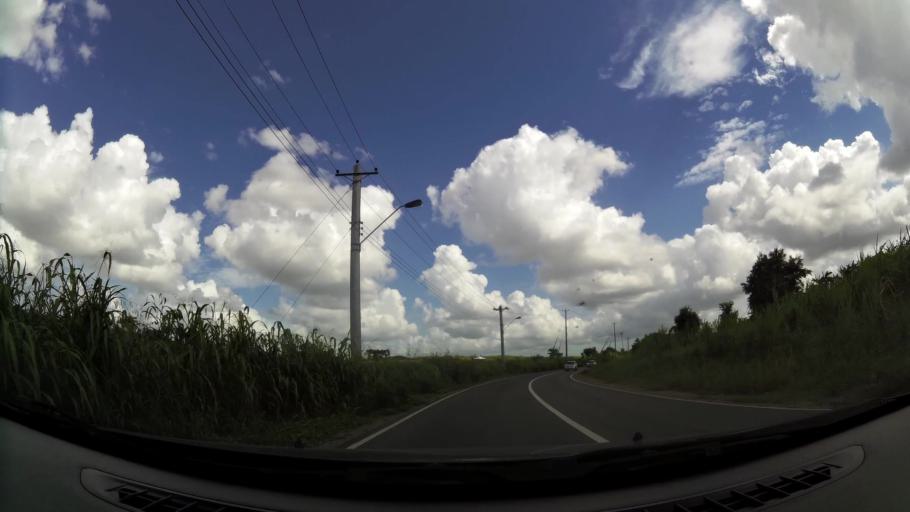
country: TT
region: Penal/Debe
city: Debe
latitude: 10.2311
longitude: -61.4816
